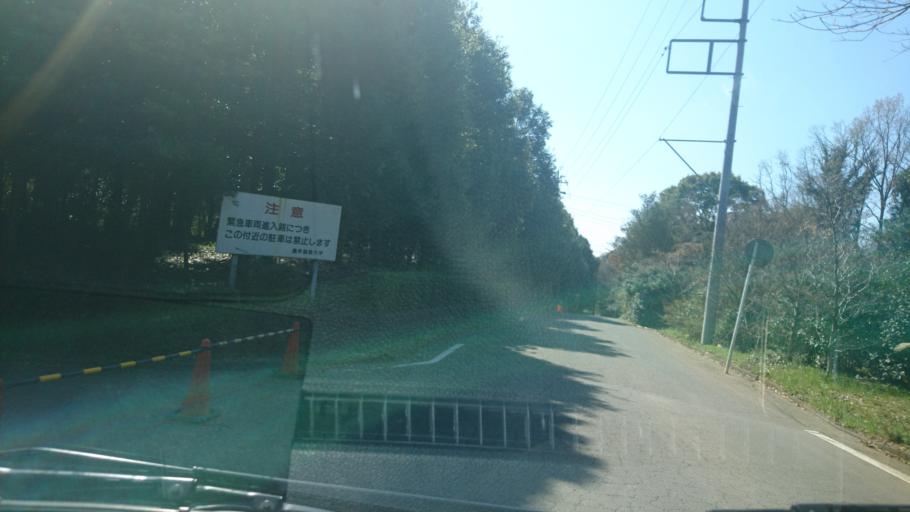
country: JP
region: Kanagawa
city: Fujisawa
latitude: 35.3878
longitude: 139.4251
